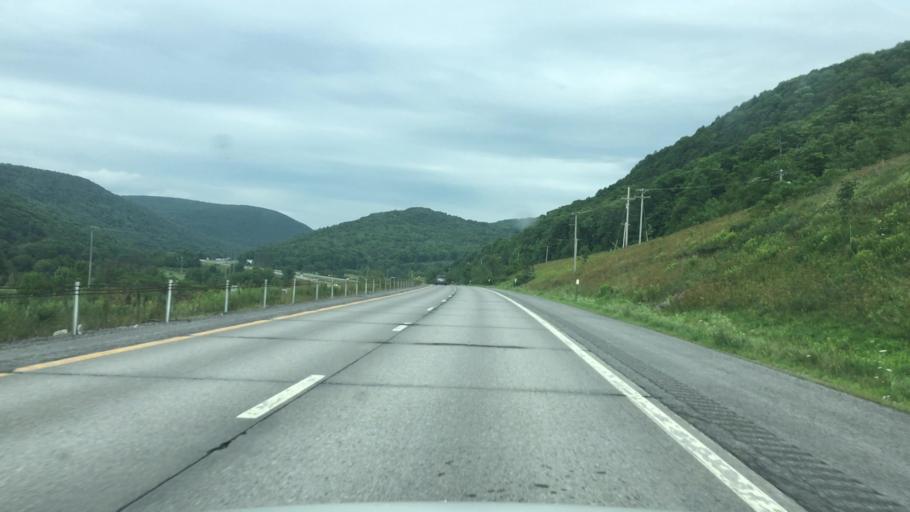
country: US
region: New York
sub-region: Otsego County
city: Worcester
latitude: 42.6186
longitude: -74.6677
